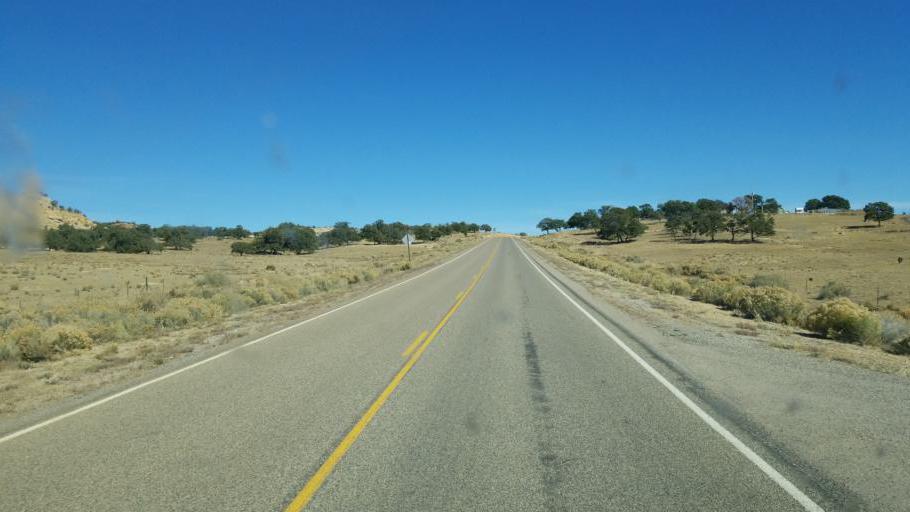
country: US
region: New Mexico
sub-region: McKinley County
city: Crownpoint
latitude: 35.5606
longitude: -108.1046
